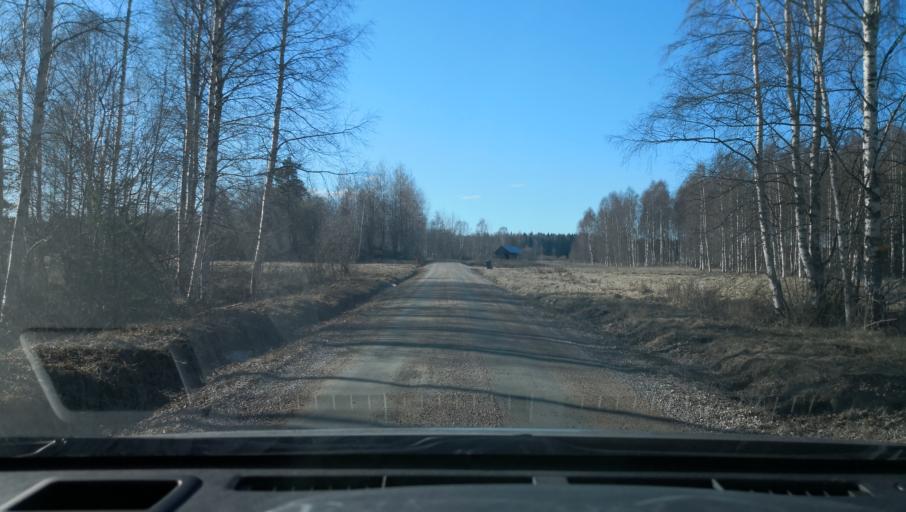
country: SE
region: Vaestmanland
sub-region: Sala Kommun
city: Sala
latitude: 60.1218
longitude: 16.6611
